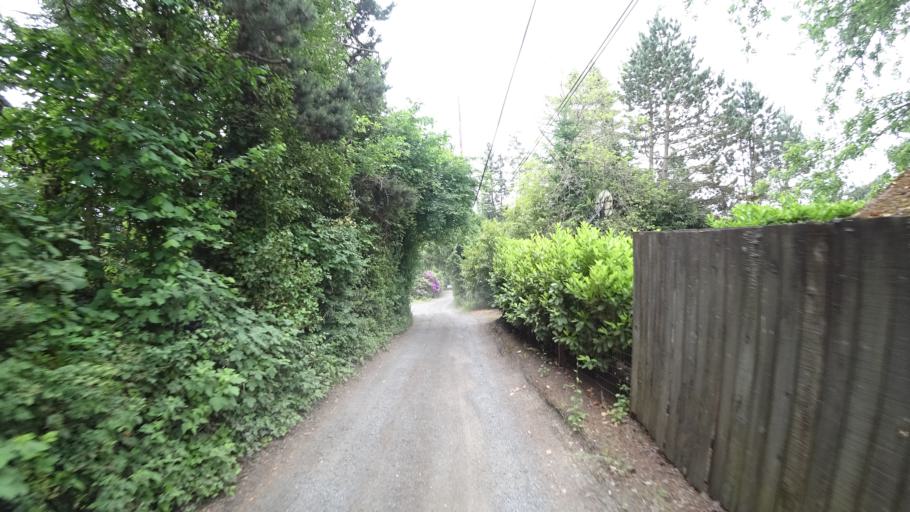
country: US
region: Oregon
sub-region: Washington County
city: Garden Home-Whitford
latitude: 45.4654
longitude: -122.7437
